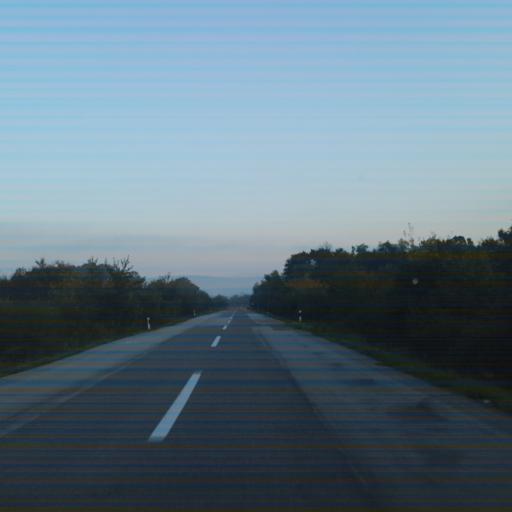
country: RS
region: Central Serbia
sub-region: Zajecarski Okrug
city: Zajecar
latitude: 43.9722
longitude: 22.2927
